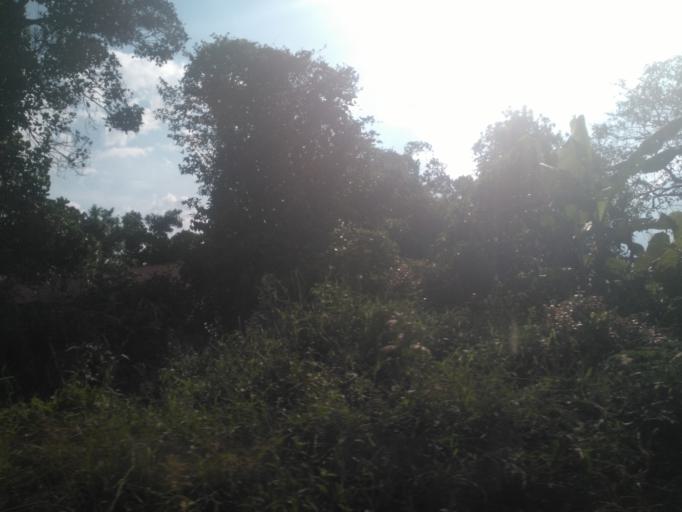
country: UG
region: Central Region
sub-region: Wakiso District
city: Wakiso
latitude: 0.2990
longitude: 32.4481
